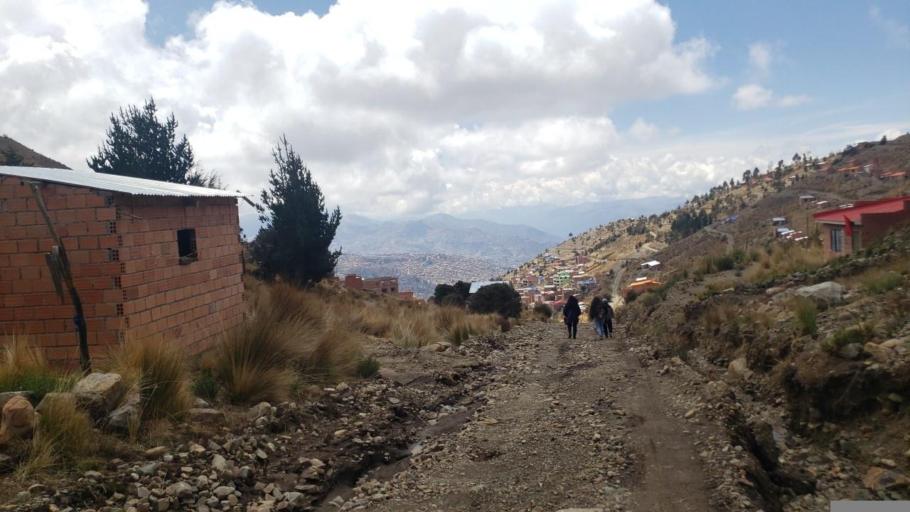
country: BO
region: La Paz
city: La Paz
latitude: -16.4630
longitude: -68.1364
